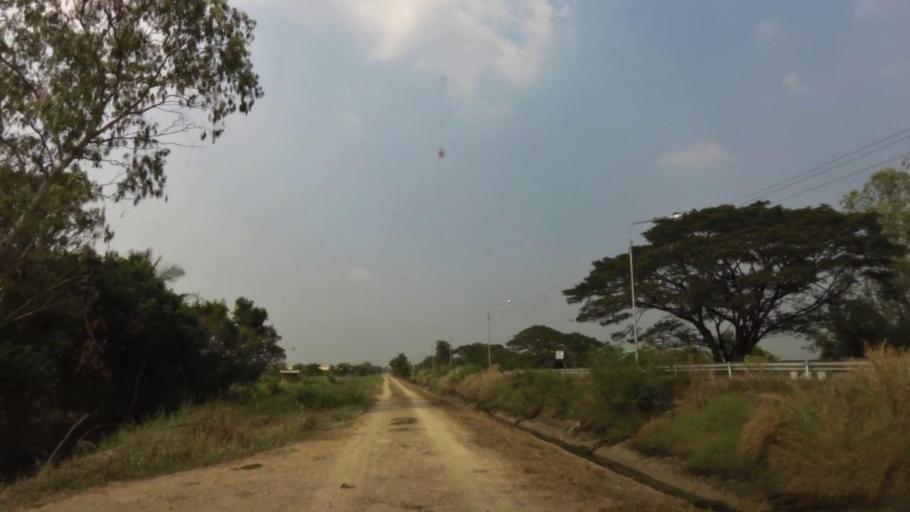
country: TH
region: Phra Nakhon Si Ayutthaya
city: Phra Nakhon Si Ayutthaya
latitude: 14.3130
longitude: 100.5617
